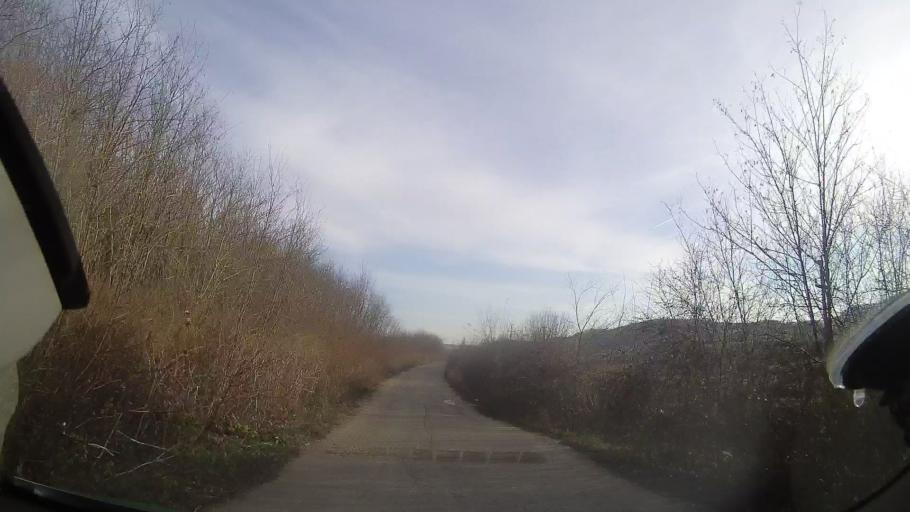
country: RO
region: Bihor
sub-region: Comuna Sarbi
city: Sarbi
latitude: 47.1812
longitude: 22.1353
